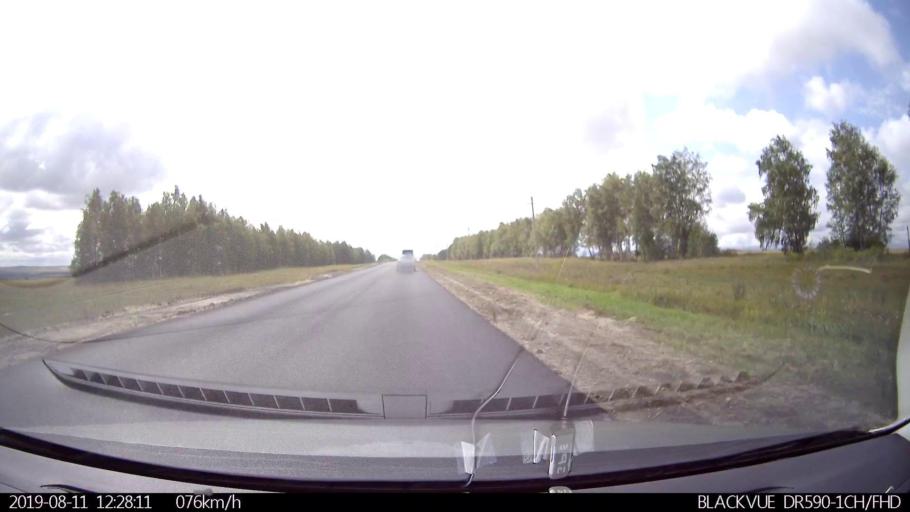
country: RU
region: Ulyanovsk
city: Ignatovka
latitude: 53.8464
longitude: 47.9137
